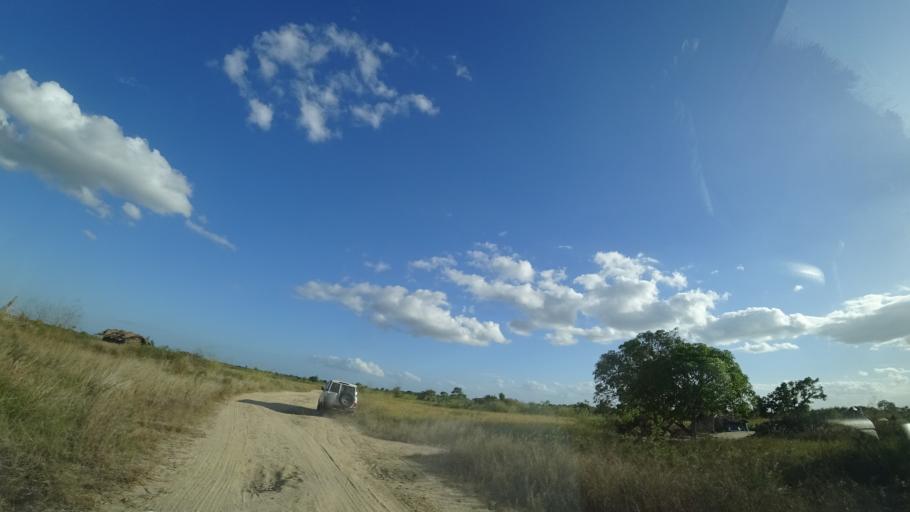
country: MZ
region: Sofala
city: Dondo
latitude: -19.4184
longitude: 34.5651
